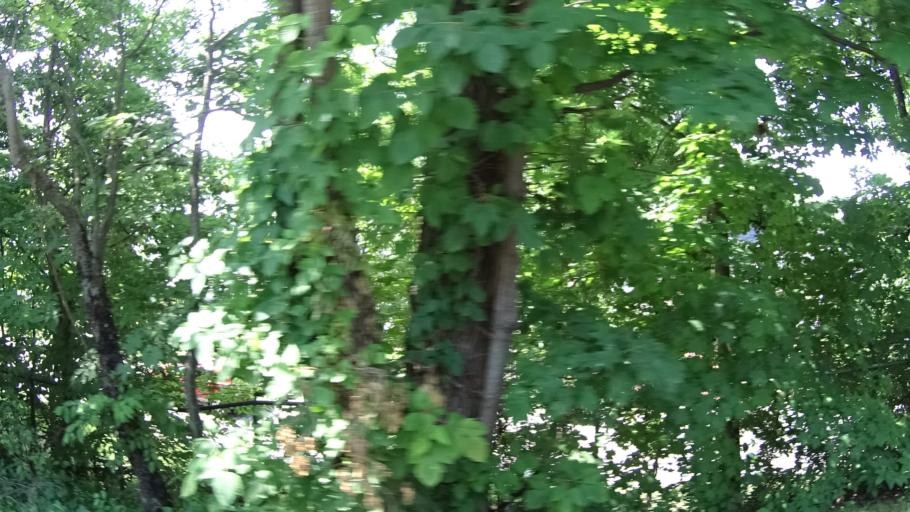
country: US
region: Ohio
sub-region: Lorain County
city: Vermilion
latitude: 41.4252
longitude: -82.3571
